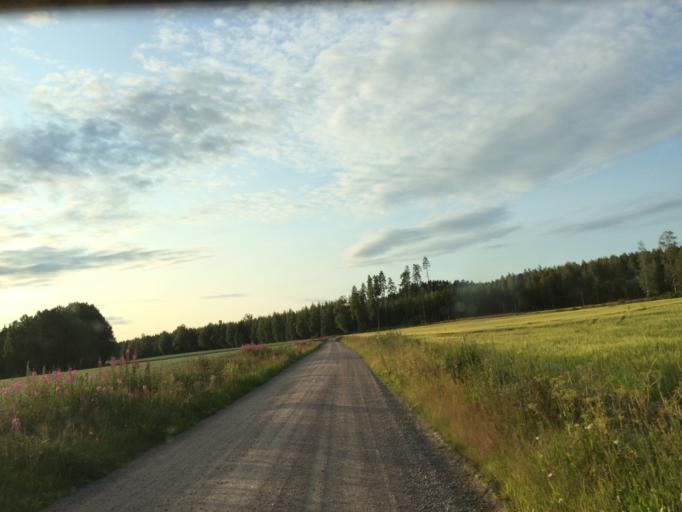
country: FI
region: Haeme
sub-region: Haemeenlinna
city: Janakkala
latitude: 60.8886
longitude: 24.6176
